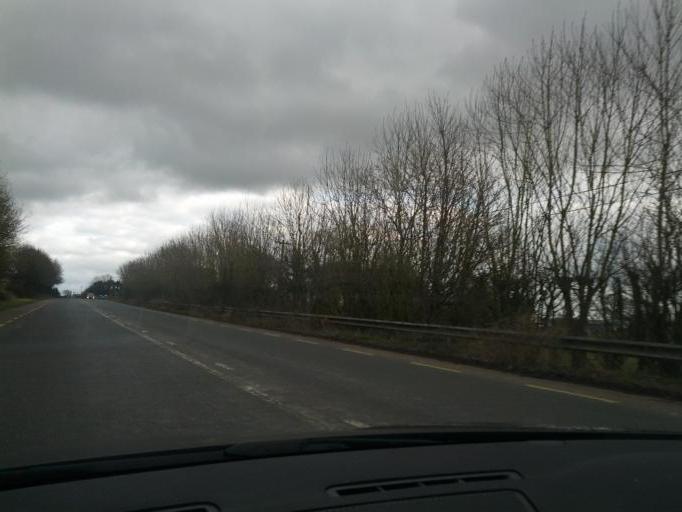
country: IE
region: Leinster
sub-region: An Iarmhi
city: Moate
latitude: 53.3968
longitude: -7.6610
